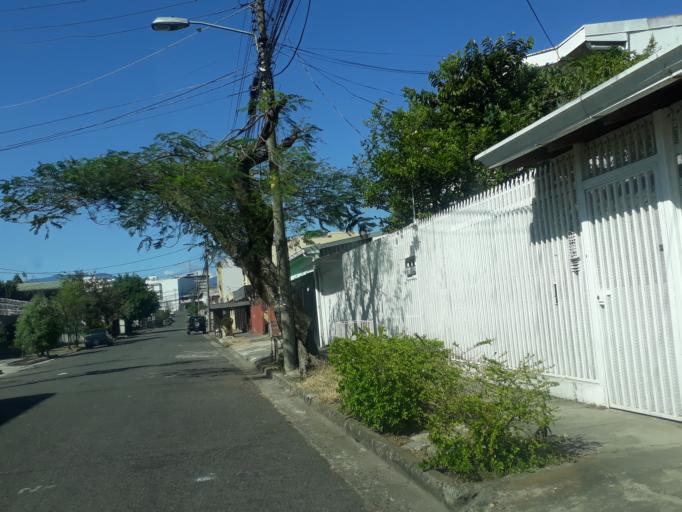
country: CR
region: San Jose
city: San Jose
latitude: 9.9289
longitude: -84.0973
